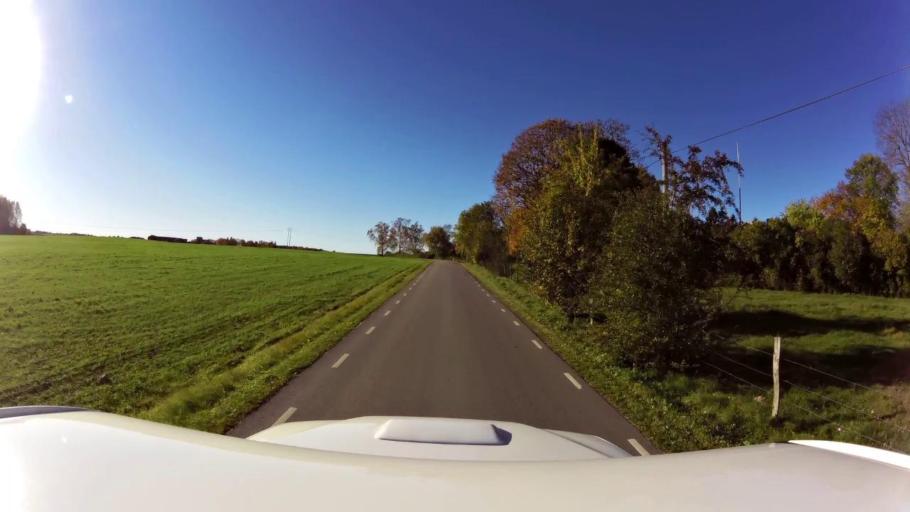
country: SE
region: OEstergoetland
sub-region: Linkopings Kommun
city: Ljungsbro
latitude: 58.5184
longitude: 15.4205
